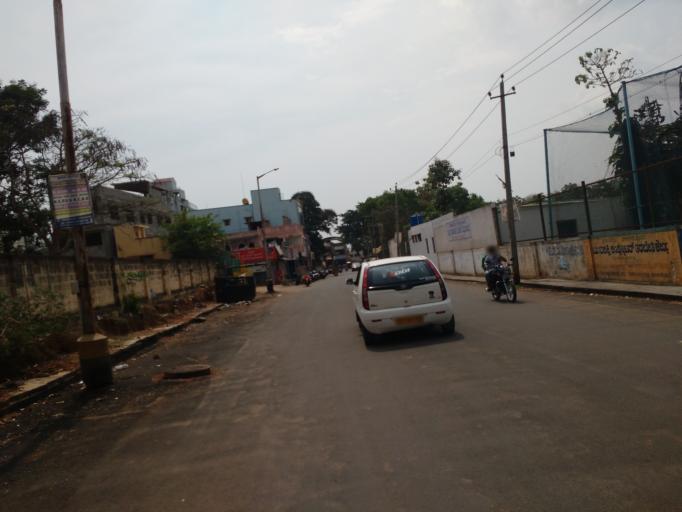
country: IN
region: Karnataka
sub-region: Hassan
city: Hassan
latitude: 13.0160
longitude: 76.1017
